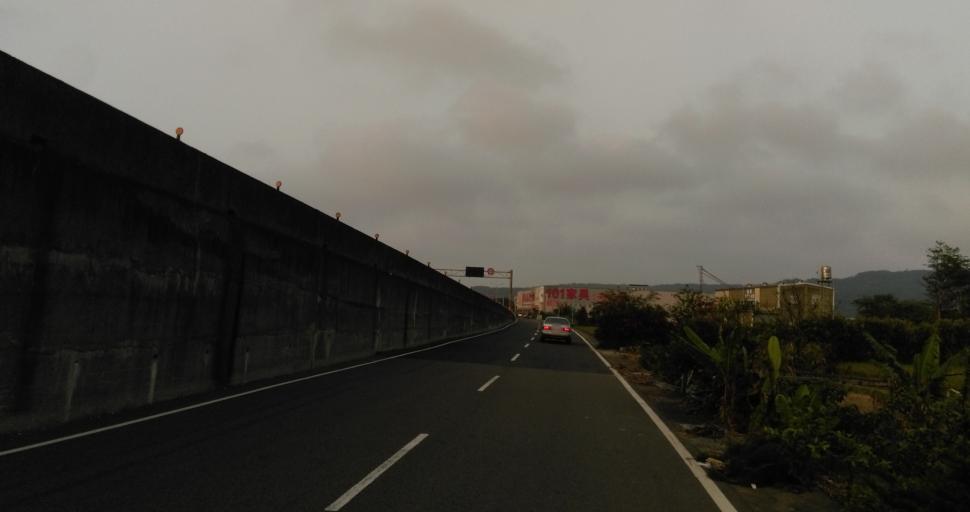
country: TW
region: Taiwan
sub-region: Hsinchu
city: Zhubei
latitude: 24.8635
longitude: 120.9525
